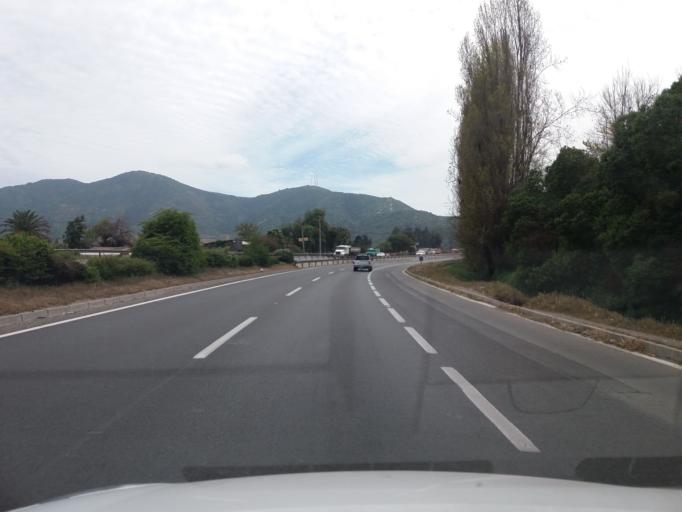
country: CL
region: Valparaiso
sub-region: Provincia de Quillota
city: Hacienda La Calera
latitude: -32.7682
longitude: -71.1923
